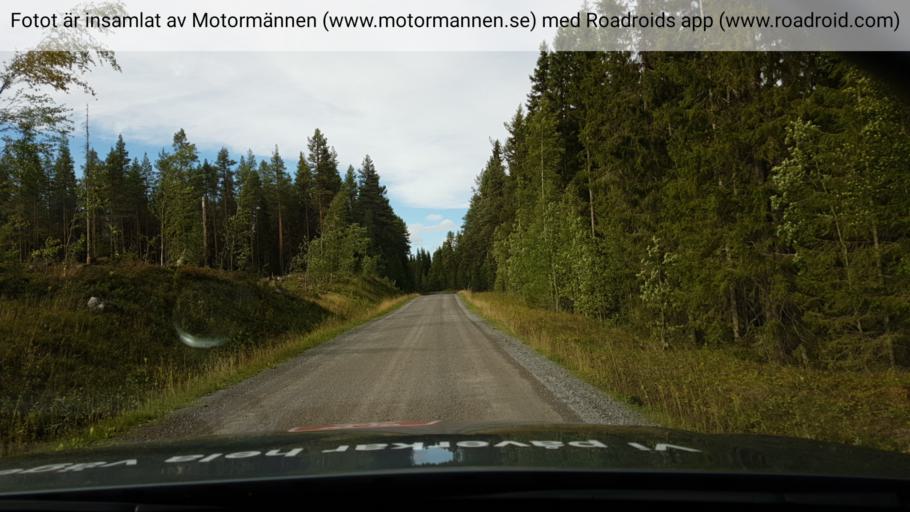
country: SE
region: Jaemtland
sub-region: Braecke Kommun
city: Braecke
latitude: 63.2725
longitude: 15.3768
